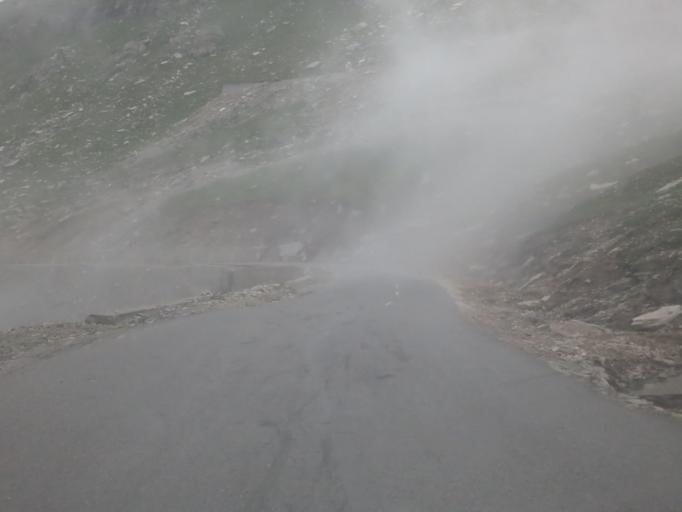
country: IN
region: Himachal Pradesh
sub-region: Kulu
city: Manali
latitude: 32.3641
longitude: 77.2418
